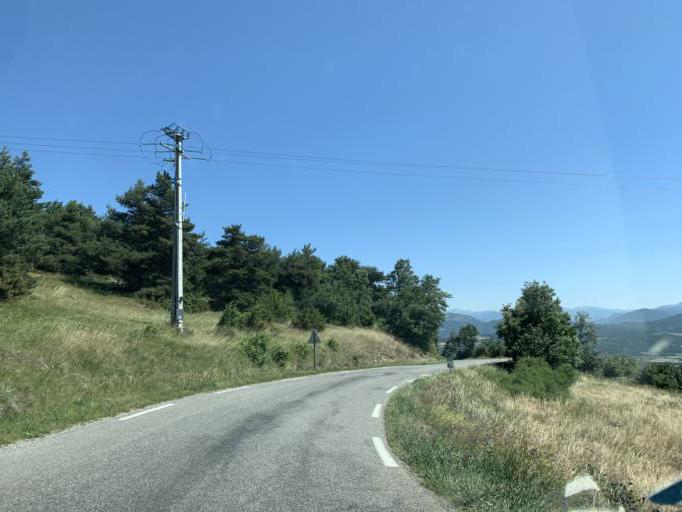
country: FR
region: Provence-Alpes-Cote d'Azur
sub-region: Departement des Hautes-Alpes
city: La Batie-Neuve
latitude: 44.6032
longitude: 6.1430
